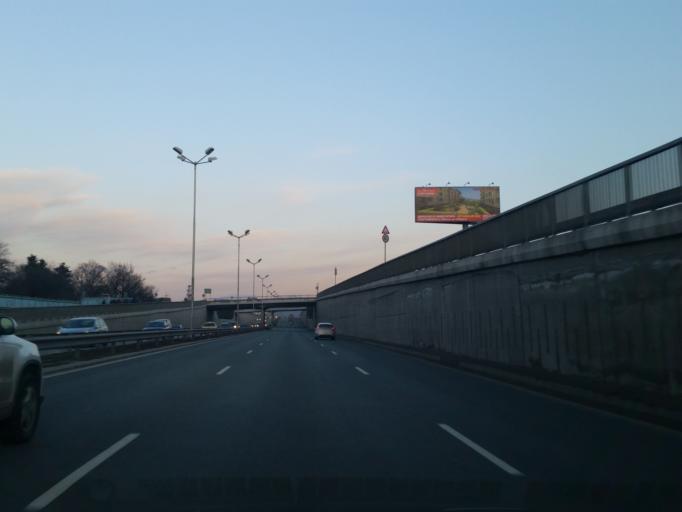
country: BG
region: Sofia-Capital
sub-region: Stolichna Obshtina
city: Sofia
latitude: 42.6426
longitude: 23.3100
